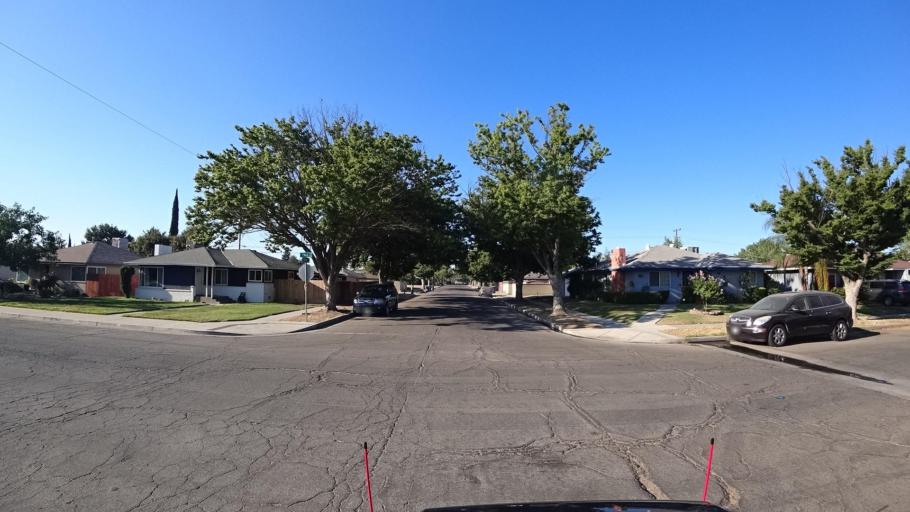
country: US
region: California
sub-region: Fresno County
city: Fresno
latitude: 36.7702
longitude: -119.8311
